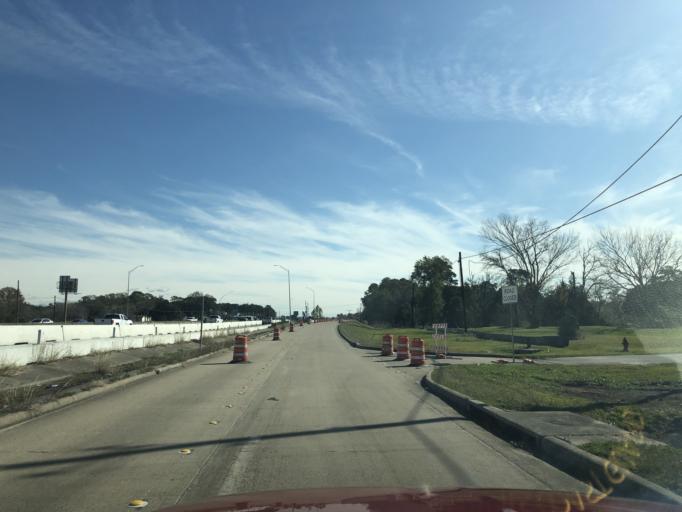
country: US
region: Texas
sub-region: Galveston County
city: Dickinson
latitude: 29.4466
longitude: -95.0754
